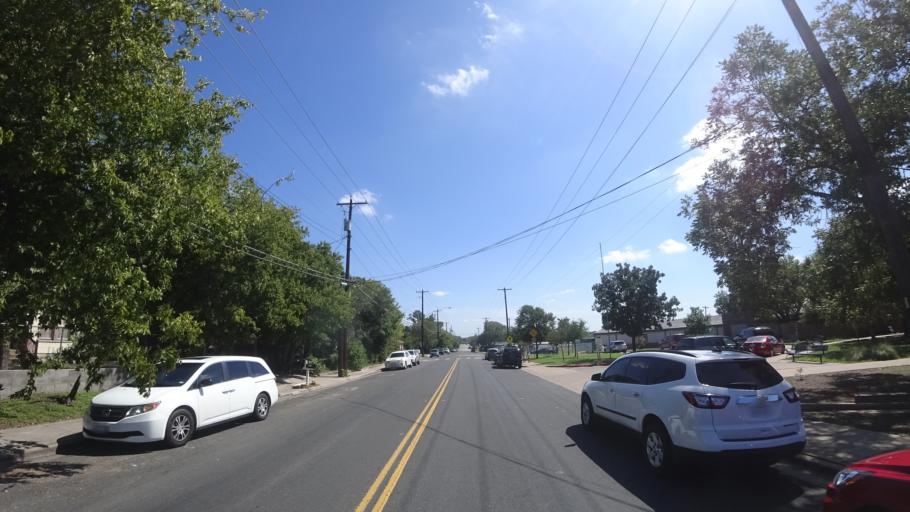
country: US
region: Texas
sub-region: Travis County
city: Austin
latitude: 30.3154
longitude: -97.6909
